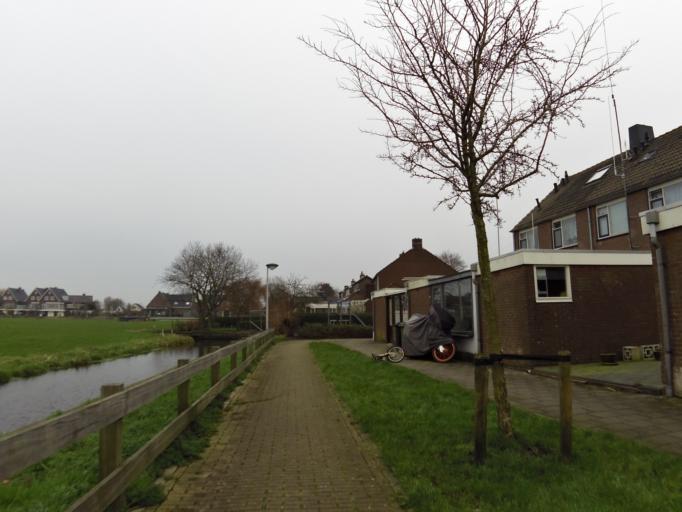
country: NL
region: South Holland
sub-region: Gemeente Leiderdorp
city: Leiderdorp
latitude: 52.1943
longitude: 4.5798
